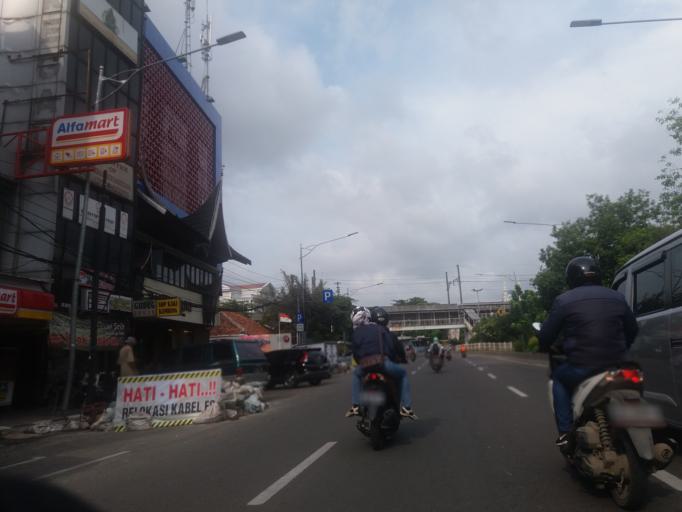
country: ID
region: Jakarta Raya
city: Jakarta
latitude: -6.1678
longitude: 106.8294
